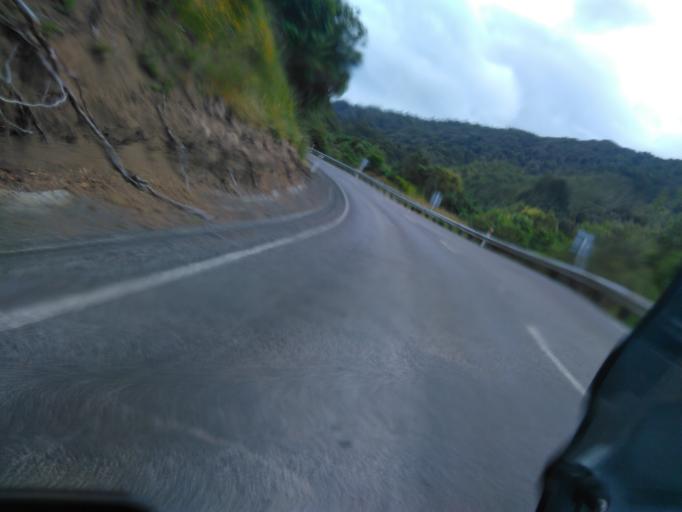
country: NZ
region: Bay of Plenty
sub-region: Opotiki District
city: Opotiki
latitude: -38.3455
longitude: 177.4477
